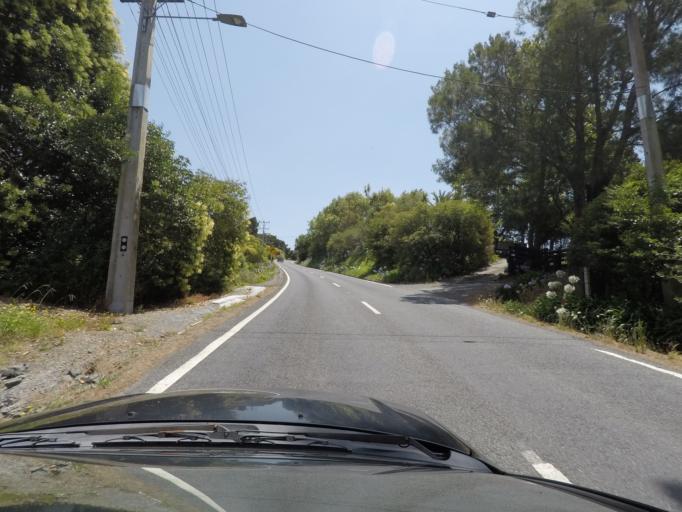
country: NZ
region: Auckland
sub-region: Auckland
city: Warkworth
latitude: -36.3923
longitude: 174.6615
